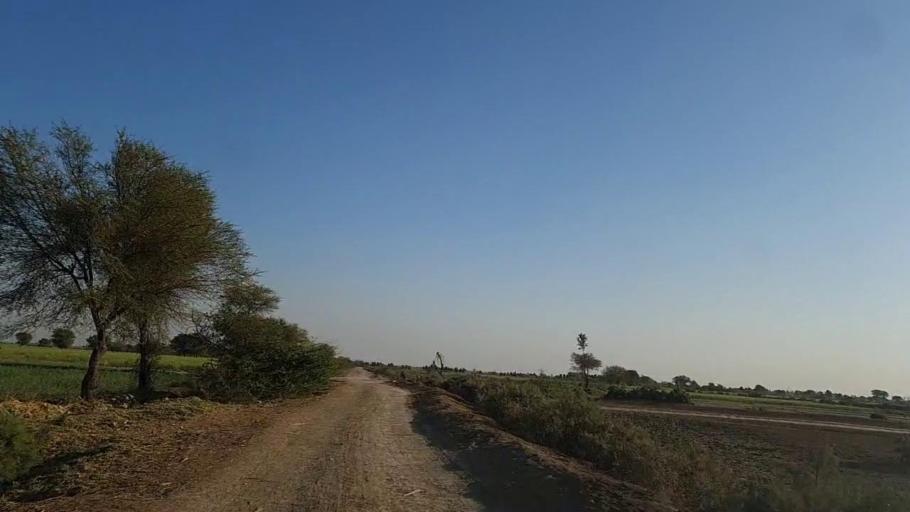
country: PK
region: Sindh
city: Samaro
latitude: 25.3359
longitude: 69.4111
